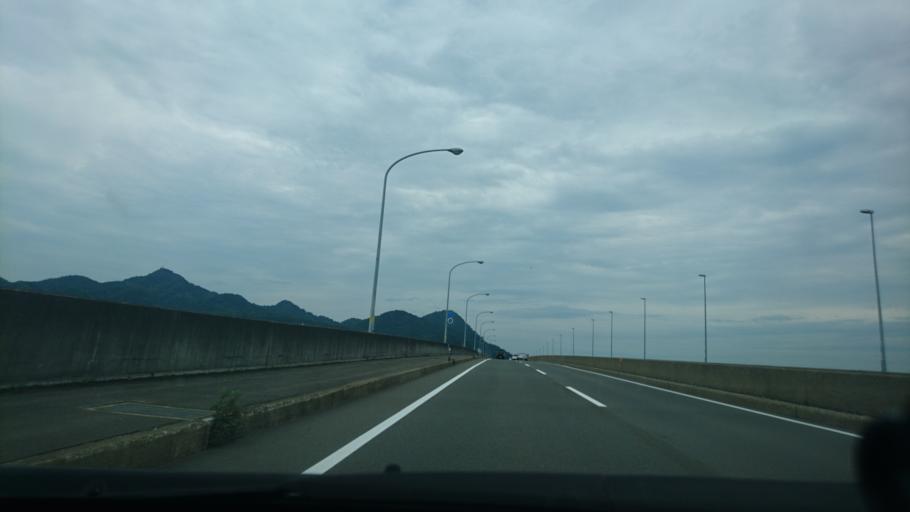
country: JP
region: Akita
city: Omagari
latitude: 39.4760
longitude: 140.4703
